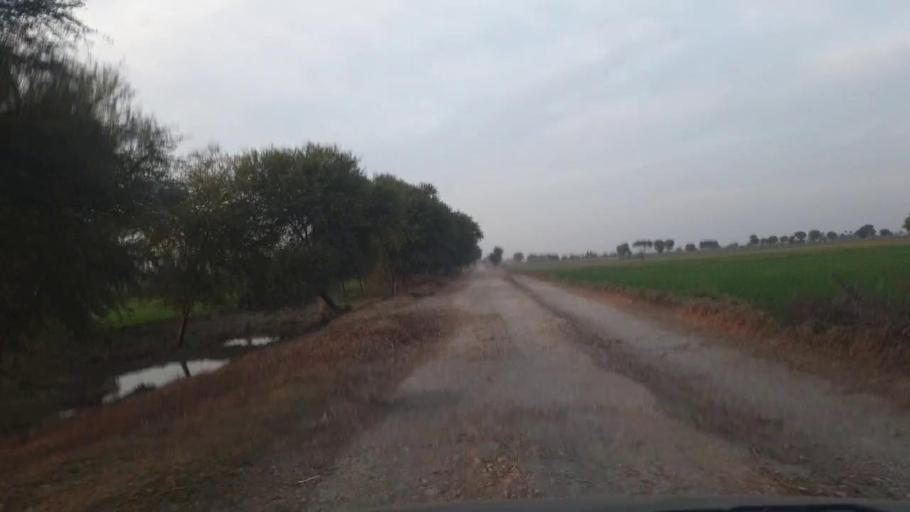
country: PK
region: Sindh
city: Shahpur Chakar
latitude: 26.0682
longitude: 68.5331
